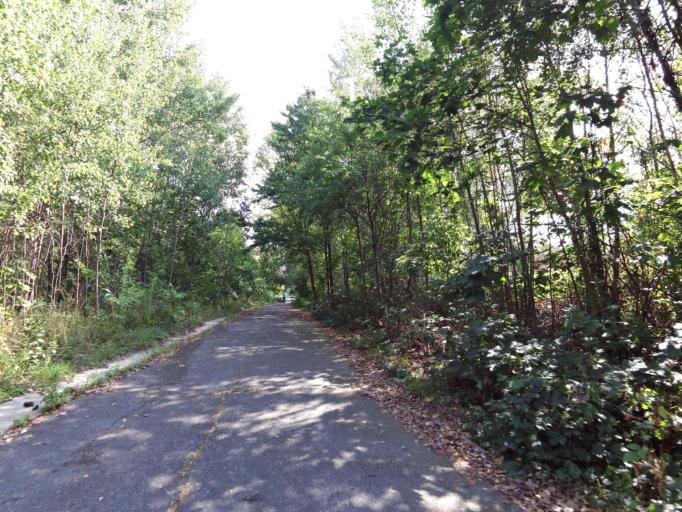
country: DE
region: Berlin
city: Lichtenrade
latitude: 52.3771
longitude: 13.3990
